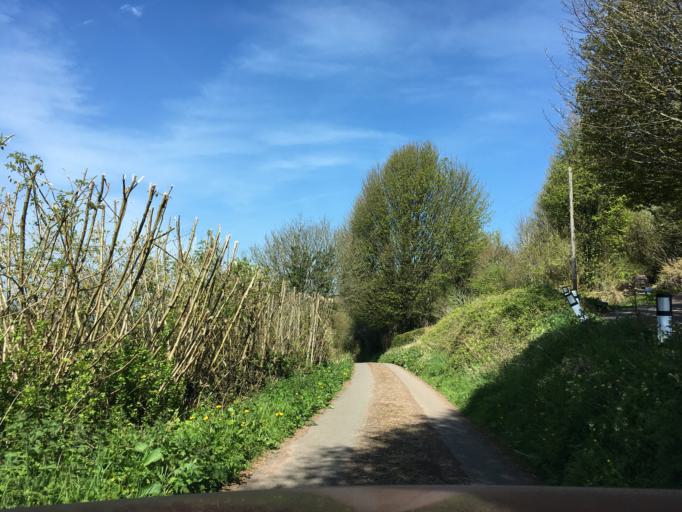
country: GB
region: Wales
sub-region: Monmouthshire
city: Llangwm
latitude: 51.6833
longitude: -2.8116
